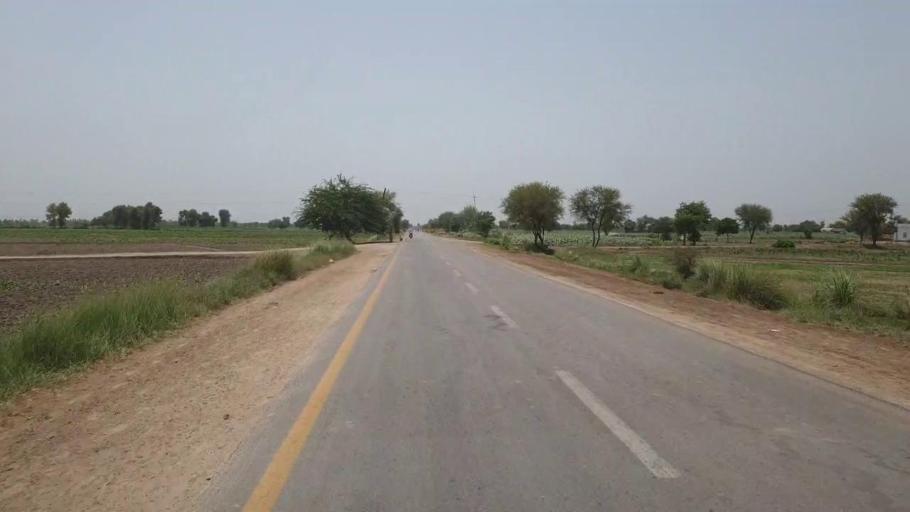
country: PK
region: Sindh
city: Moro
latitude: 26.6065
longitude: 68.0501
